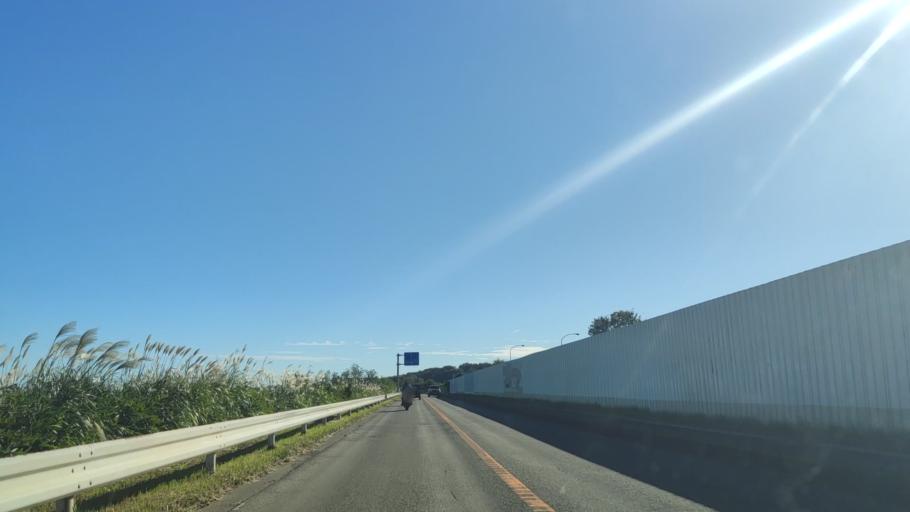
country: JP
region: Kanagawa
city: Zama
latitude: 35.5043
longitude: 139.3728
